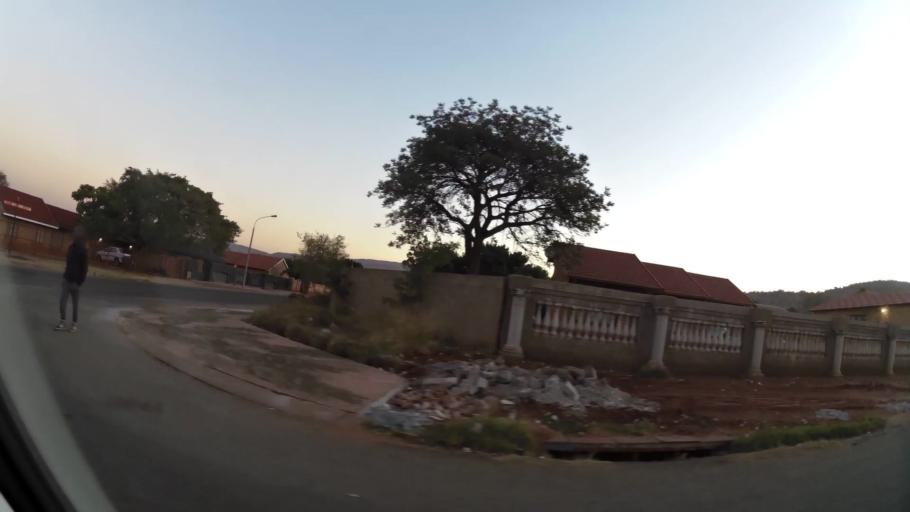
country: ZA
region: North-West
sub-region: Bojanala Platinum District Municipality
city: Rustenburg
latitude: -25.6617
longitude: 27.2098
